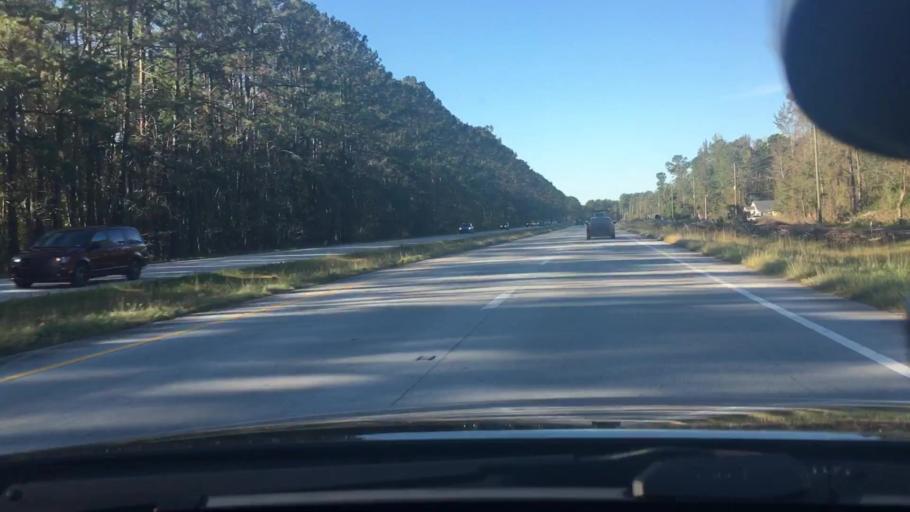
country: US
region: North Carolina
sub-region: Craven County
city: Neuse Forest
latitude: 34.9808
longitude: -76.9775
